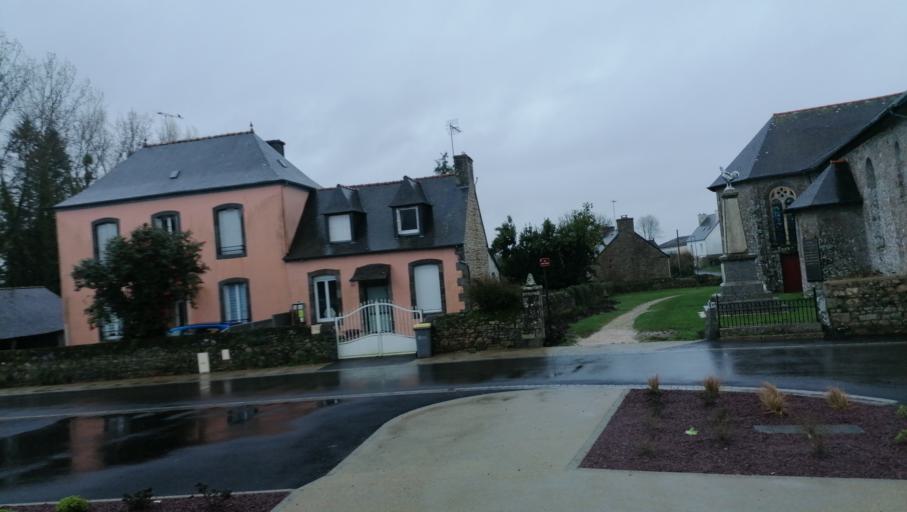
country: FR
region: Brittany
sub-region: Departement des Cotes-d'Armor
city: Plouagat
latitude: 48.4830
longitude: -2.9603
